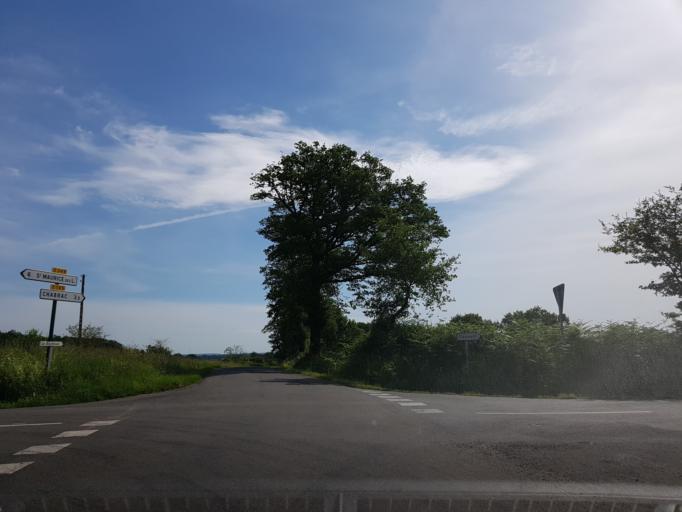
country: FR
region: Poitou-Charentes
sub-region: Departement de la Charente
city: Exideuil
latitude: 45.9180
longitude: 0.6993
